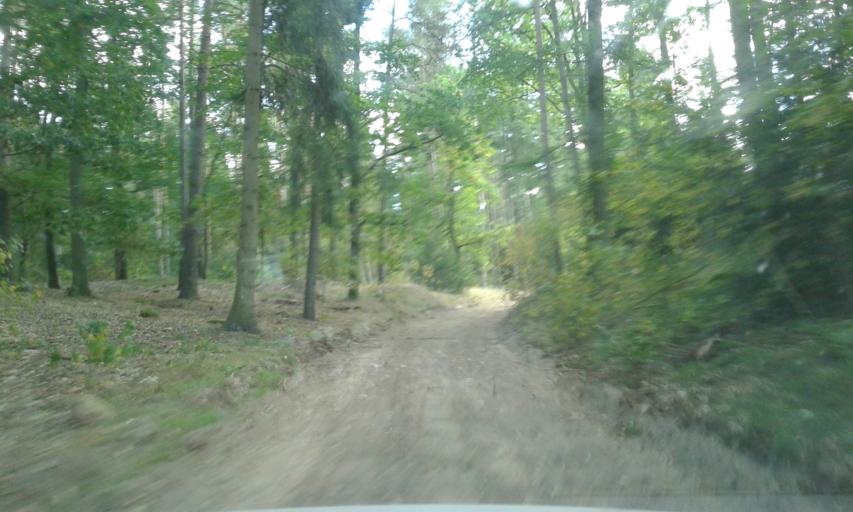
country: PL
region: West Pomeranian Voivodeship
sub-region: Powiat stargardzki
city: Dolice
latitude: 53.2342
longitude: 15.2441
